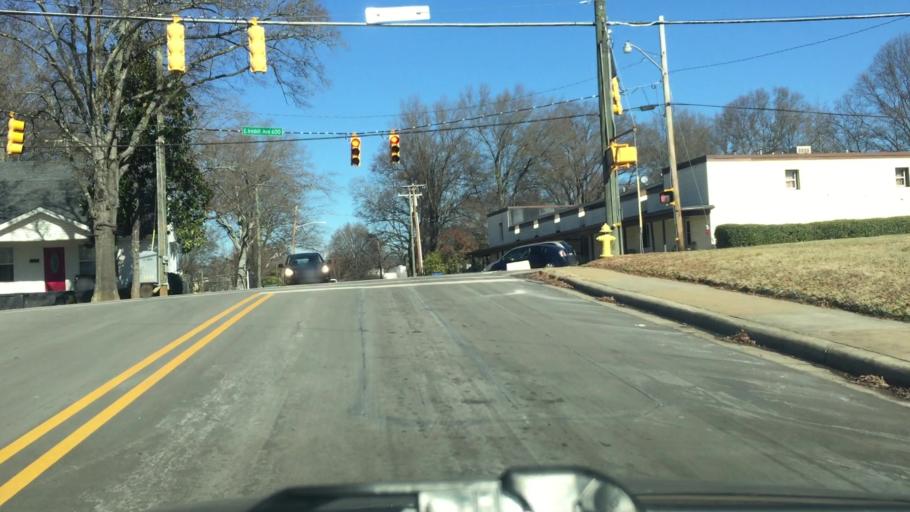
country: US
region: North Carolina
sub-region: Iredell County
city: Mooresville
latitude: 35.5825
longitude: -80.8038
